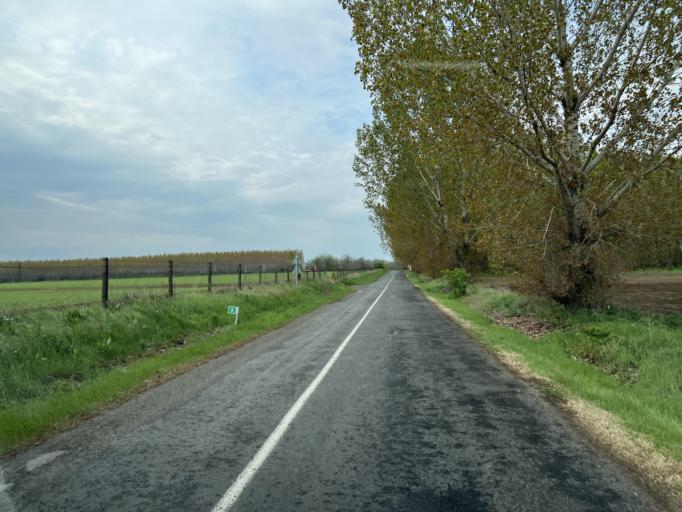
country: HU
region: Pest
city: Danszentmiklos
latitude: 47.1955
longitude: 19.5532
